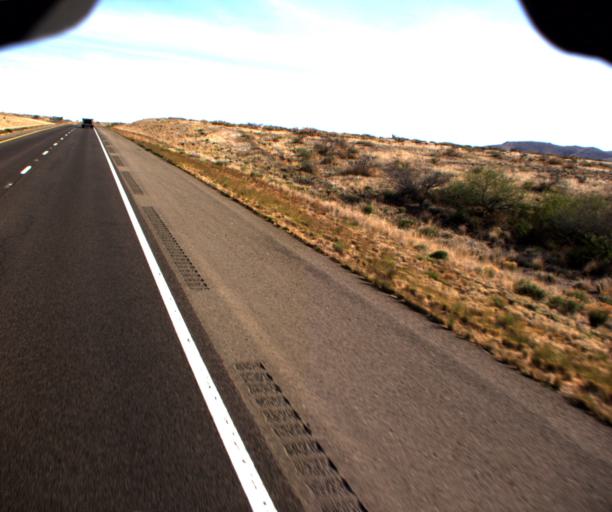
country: US
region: Arizona
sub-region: Cochise County
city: Willcox
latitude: 32.3849
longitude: -109.6665
